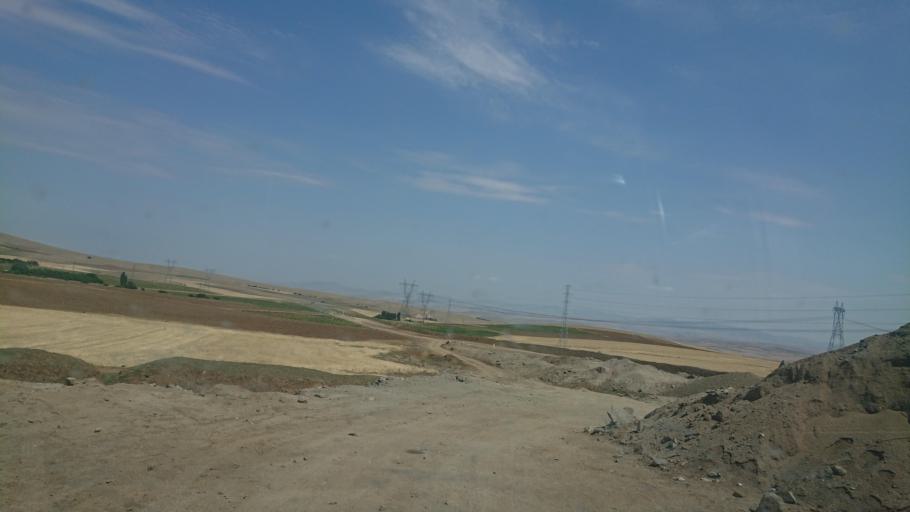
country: TR
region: Aksaray
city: Agacoren
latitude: 38.8971
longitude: 33.9260
